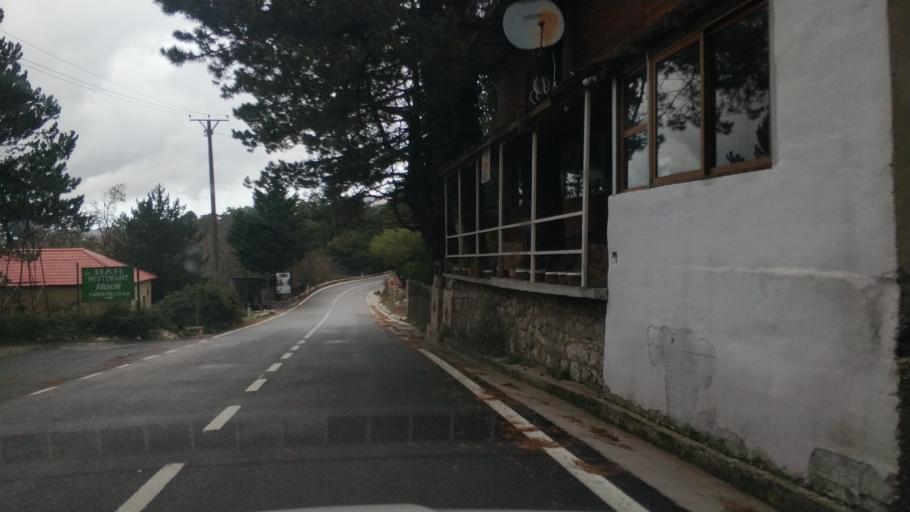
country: AL
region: Vlore
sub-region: Rrethi i Vlores
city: Brataj
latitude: 40.2159
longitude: 19.5791
